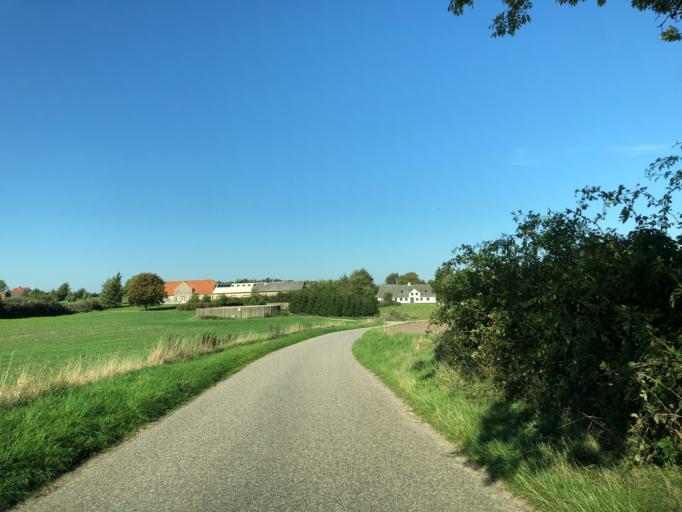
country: DK
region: South Denmark
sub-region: Sonderborg Kommune
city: Dybbol
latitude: 54.9524
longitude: 9.7289
